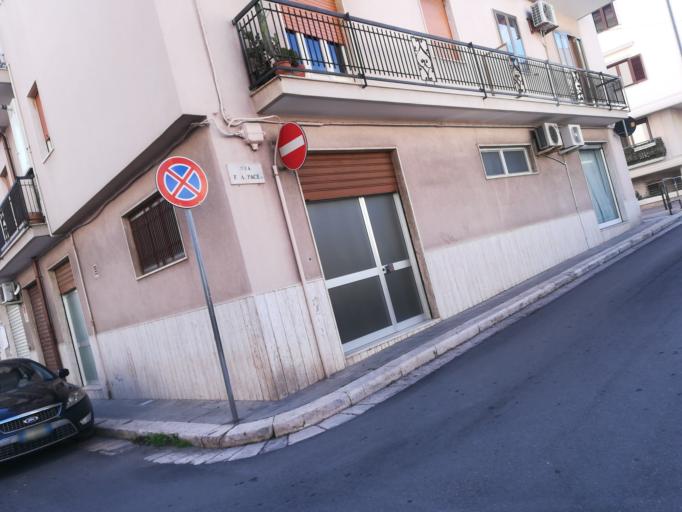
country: IT
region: Apulia
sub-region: Provincia di Bari
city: Polignano a Mare
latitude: 40.9943
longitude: 17.2230
